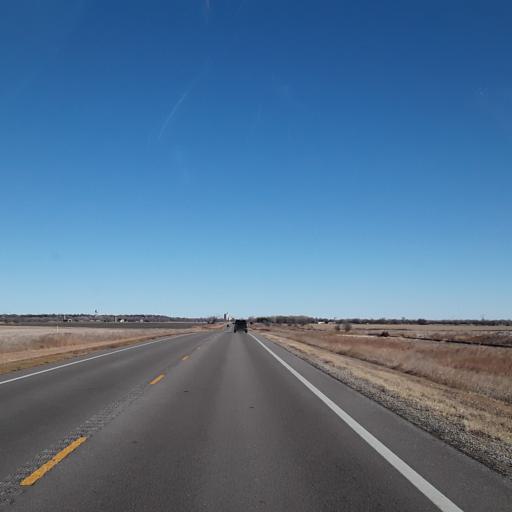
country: US
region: Kansas
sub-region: Pawnee County
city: Larned
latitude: 38.1497
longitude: -99.1364
